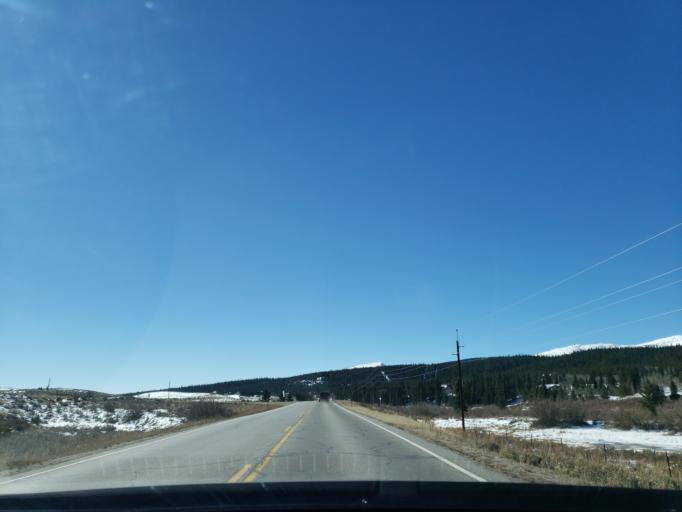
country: US
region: Colorado
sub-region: Park County
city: Fairplay
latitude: 39.3000
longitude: -106.0641
